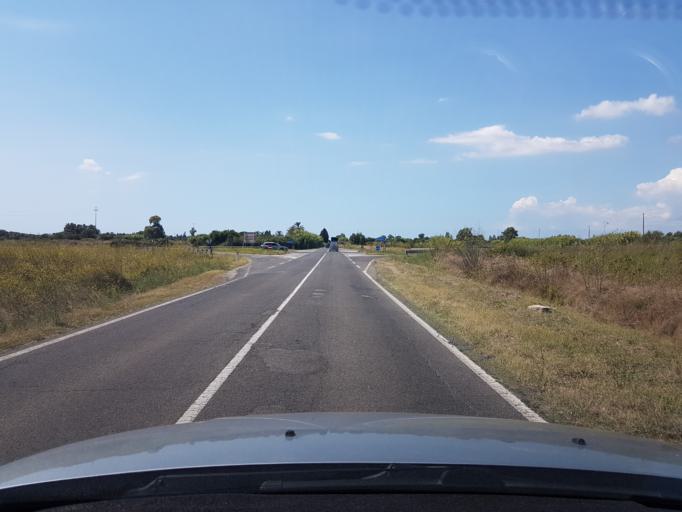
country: IT
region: Sardinia
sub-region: Provincia di Oristano
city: Donigala Fenugheddu
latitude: 39.9504
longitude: 8.5607
